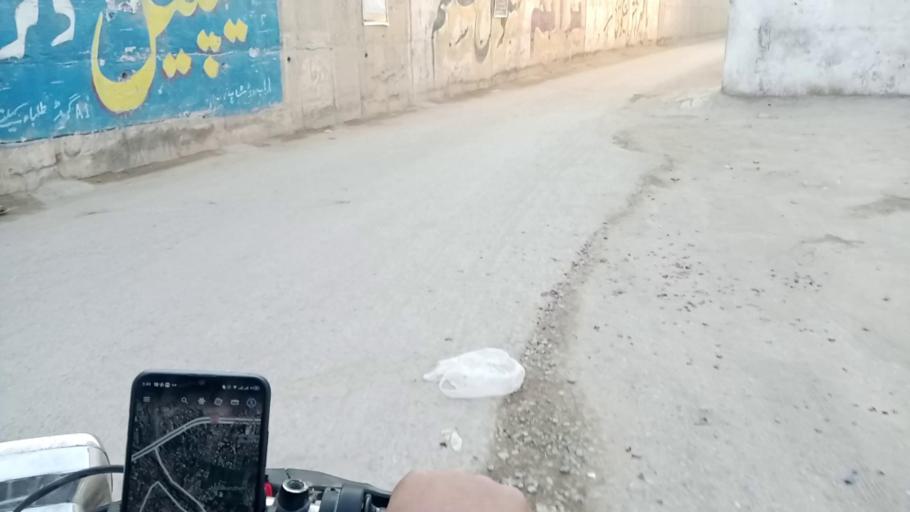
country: PK
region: Khyber Pakhtunkhwa
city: Peshawar
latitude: 34.0043
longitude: 71.4661
